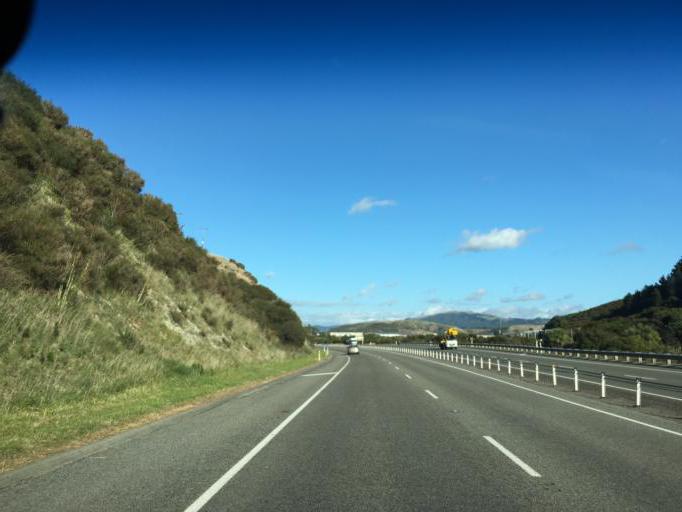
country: NZ
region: Wellington
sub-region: Porirua City
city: Porirua
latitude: -41.0703
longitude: 174.8764
